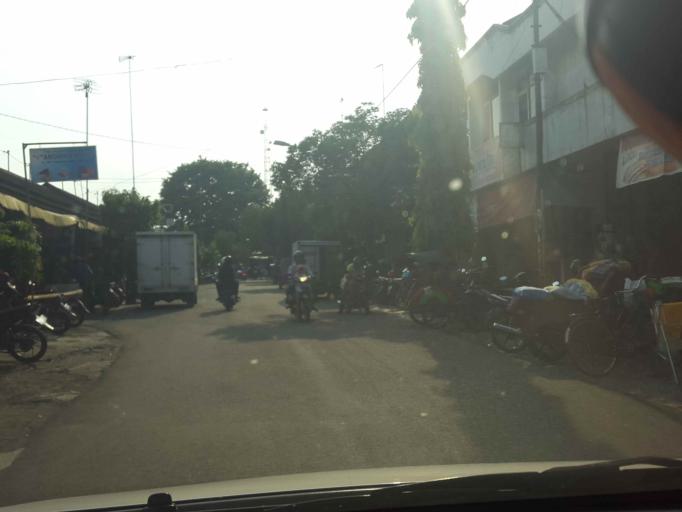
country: ID
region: Central Java
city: Sragen
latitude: -7.4287
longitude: 111.0209
